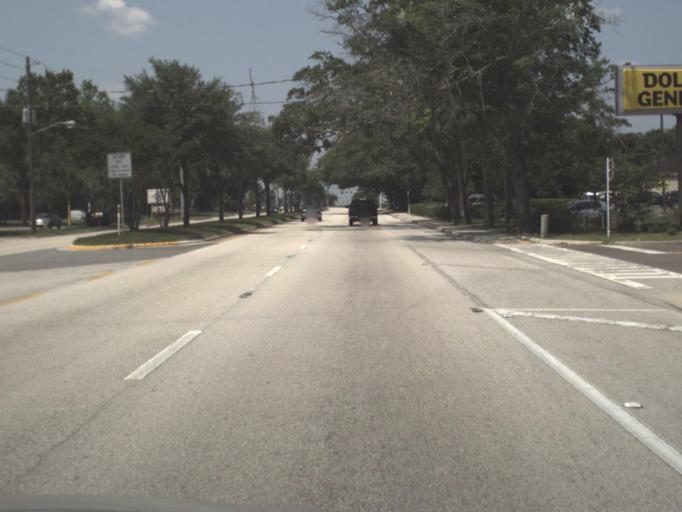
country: US
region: Florida
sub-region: Clay County
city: Bellair-Meadowbrook Terrace
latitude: 30.2874
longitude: -81.7995
